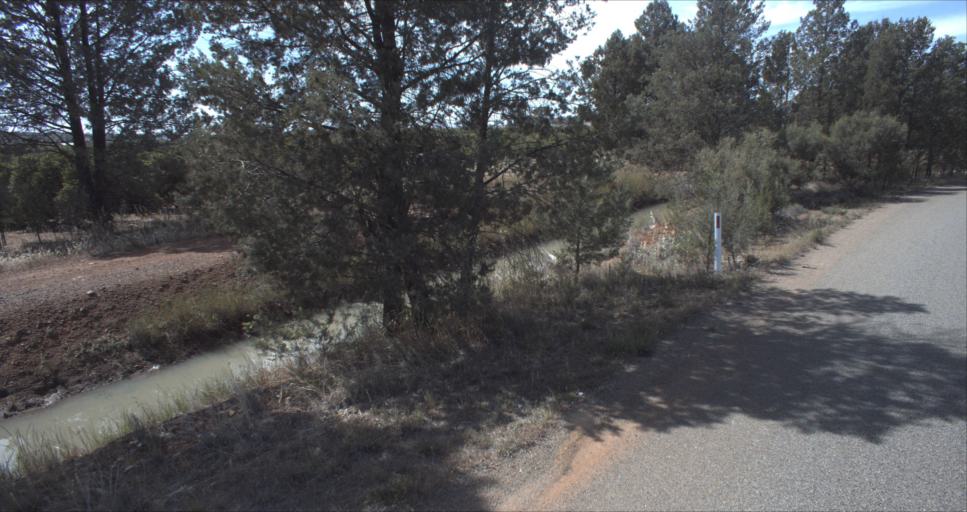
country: AU
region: New South Wales
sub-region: Leeton
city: Leeton
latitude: -34.5851
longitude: 146.4616
